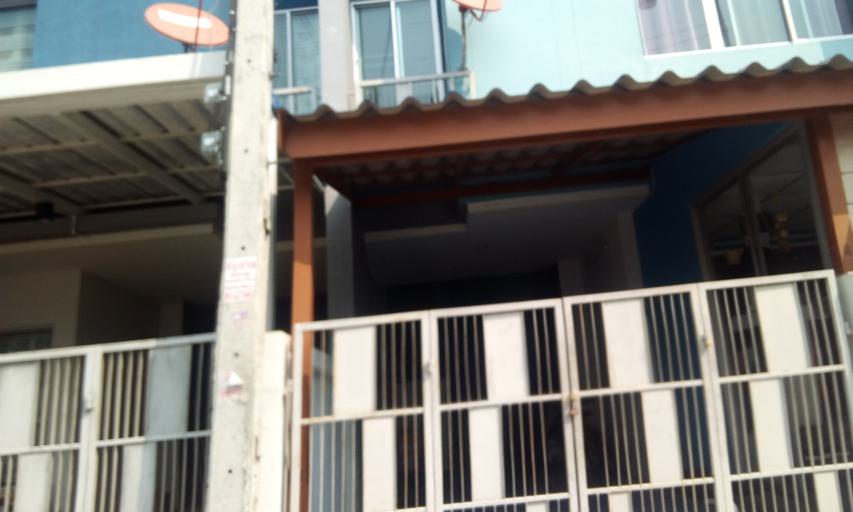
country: TH
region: Pathum Thani
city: Lam Luk Ka
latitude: 13.9374
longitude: 100.7202
